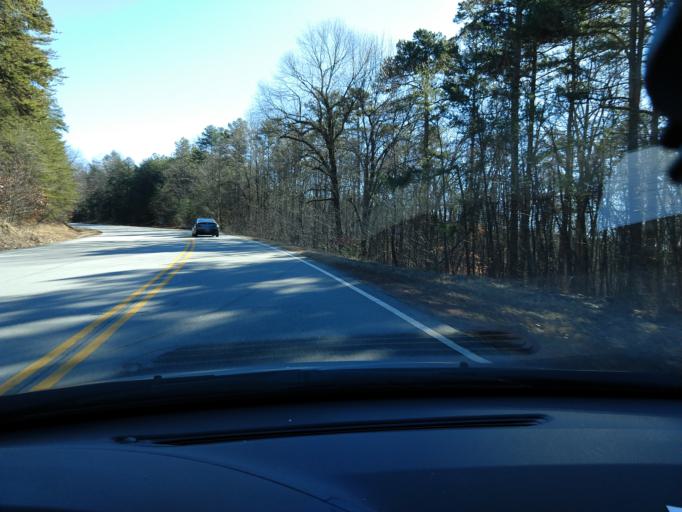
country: US
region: Georgia
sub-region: Stephens County
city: Toccoa
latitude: 34.6101
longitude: -83.3751
